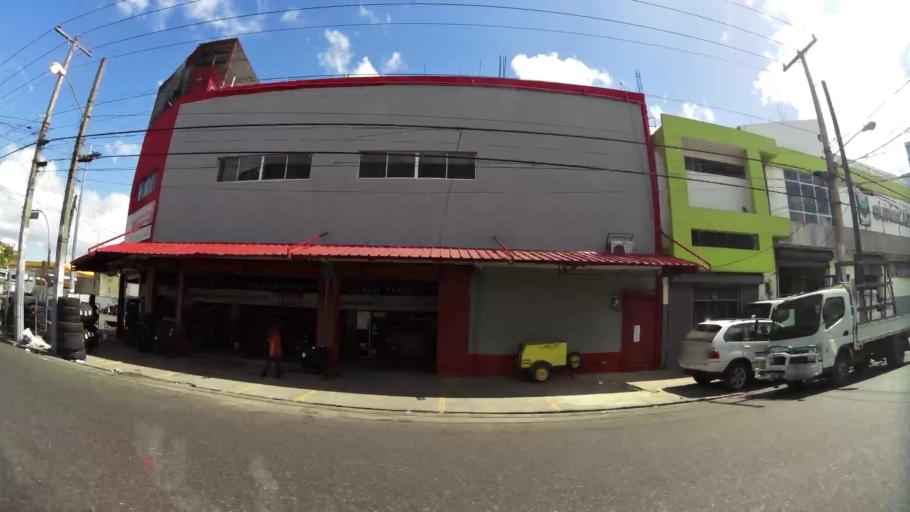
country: DO
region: Nacional
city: Ensanche Luperon
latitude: 18.4967
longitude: -69.9018
